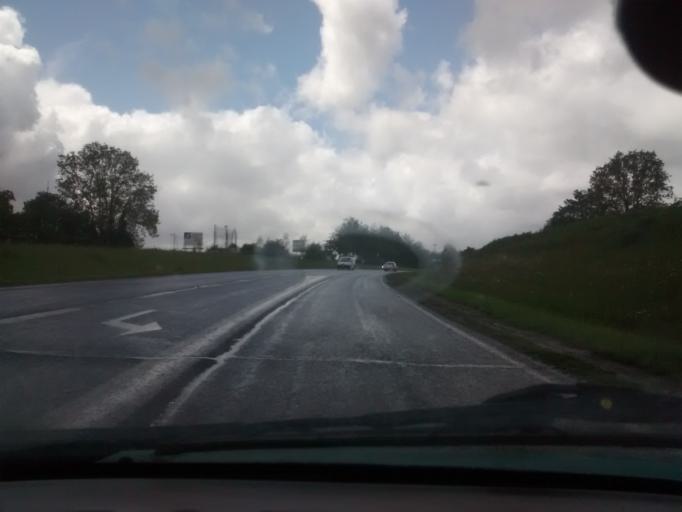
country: FR
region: Lower Normandy
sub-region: Departement de la Manche
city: Saint-Lo
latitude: 49.1070
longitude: -1.0609
